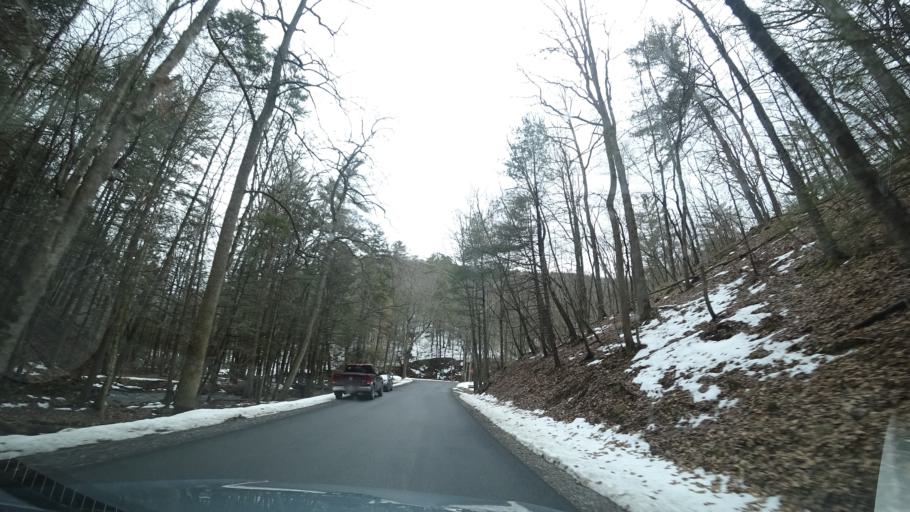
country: US
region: Virginia
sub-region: Shenandoah County
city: Basye
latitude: 38.8973
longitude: -78.9163
